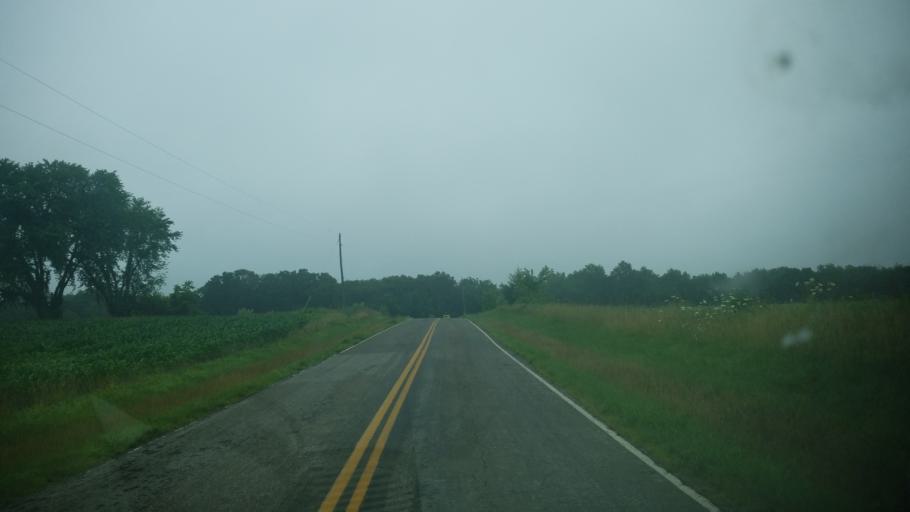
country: US
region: Missouri
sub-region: Audrain County
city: Vandalia
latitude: 39.2858
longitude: -91.3461
